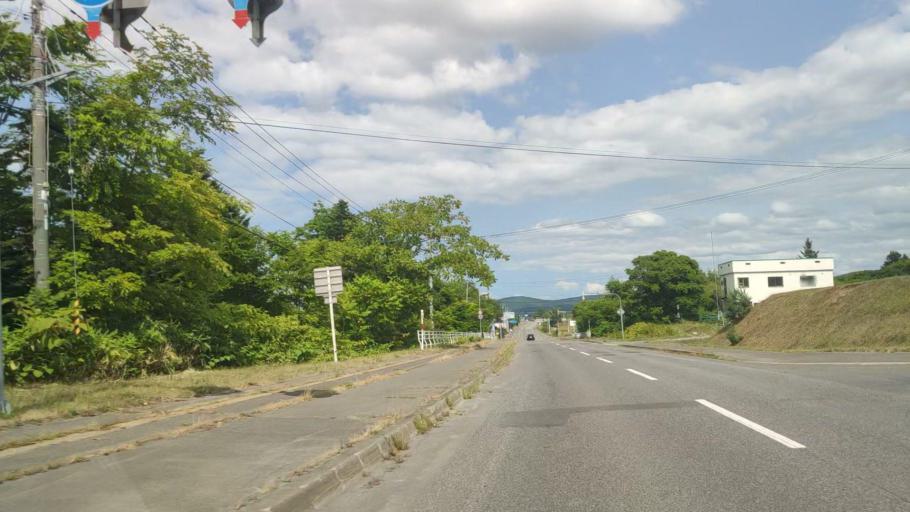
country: JP
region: Hokkaido
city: Nayoro
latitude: 44.1870
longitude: 142.4063
